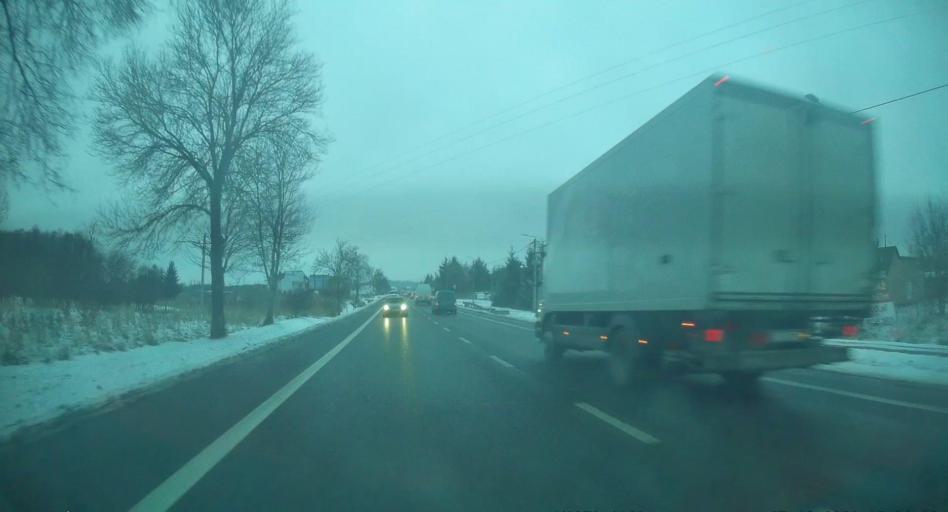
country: PL
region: Swietokrzyskie
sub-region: Powiat kielecki
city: Kostomloty Drugie
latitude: 50.9161
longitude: 20.5727
